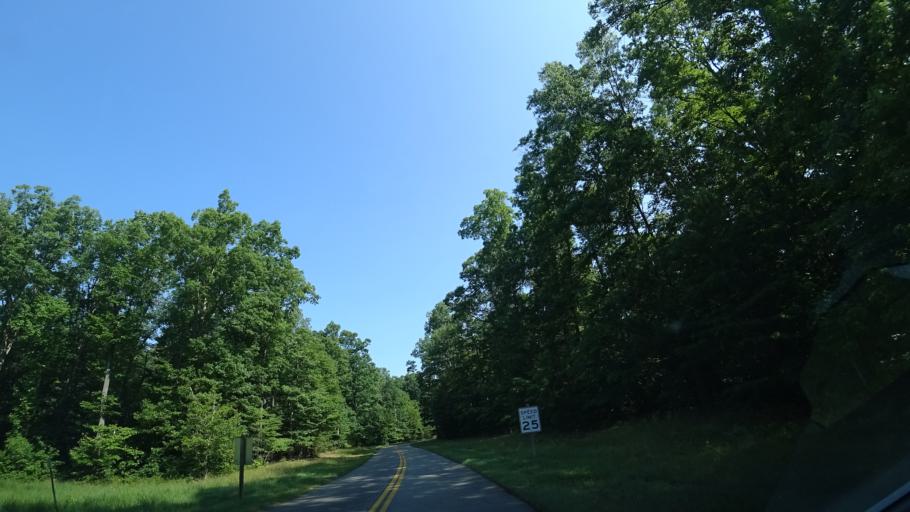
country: US
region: Virginia
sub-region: Louisa County
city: Louisa
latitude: 38.1147
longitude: -77.8182
